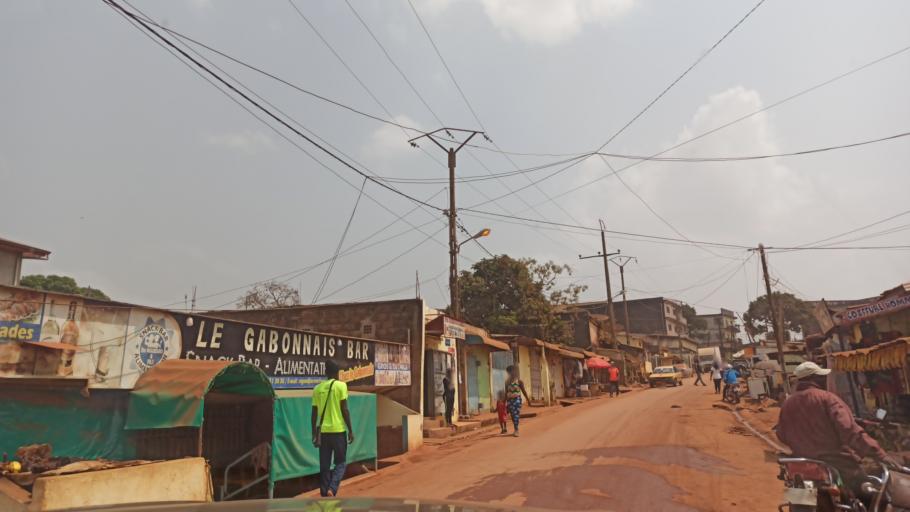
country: CM
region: Centre
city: Yaounde
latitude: 3.8853
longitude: 11.4904
